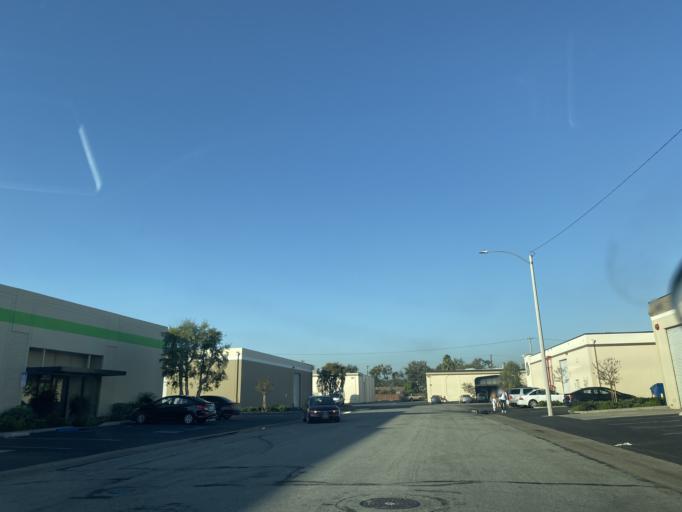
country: US
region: California
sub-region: Orange County
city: Fullerton
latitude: 33.8617
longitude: -117.9177
